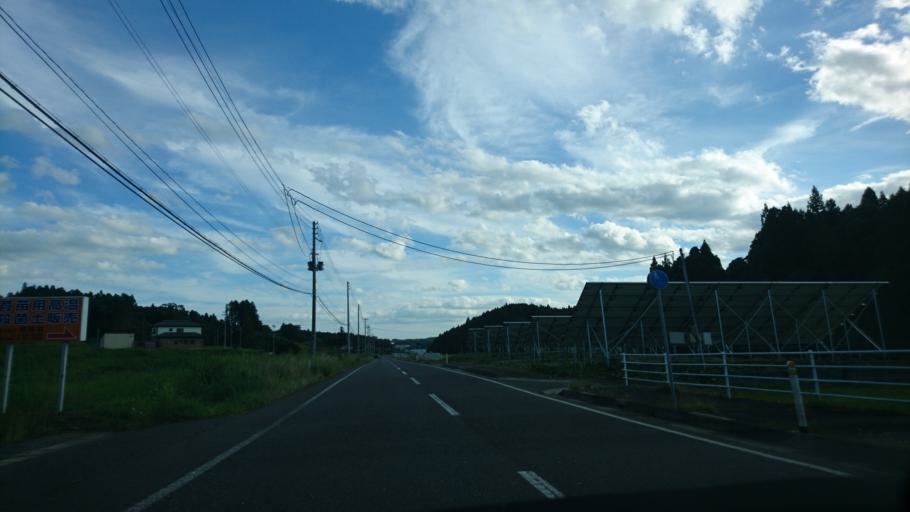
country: JP
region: Iwate
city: Ichinoseki
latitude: 38.8597
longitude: 141.1847
